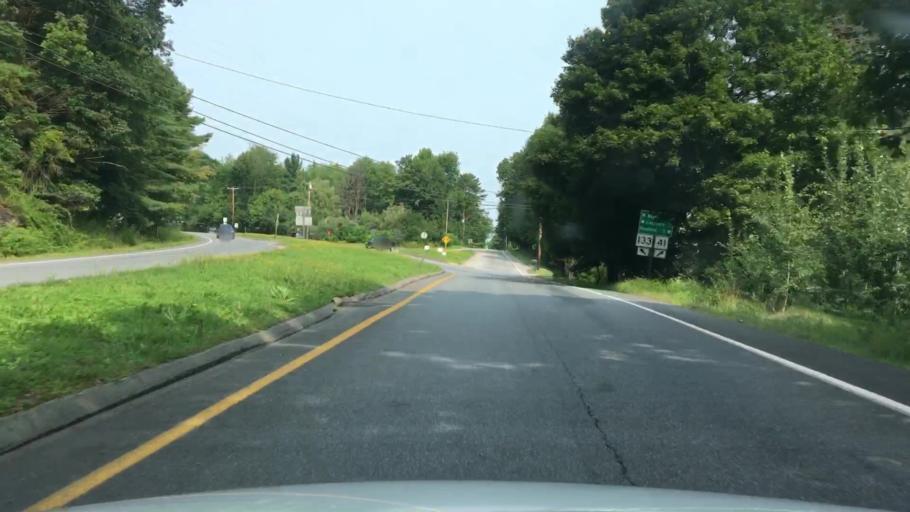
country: US
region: Maine
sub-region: Kennebec County
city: Winthrop
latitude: 44.3204
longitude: -69.9787
